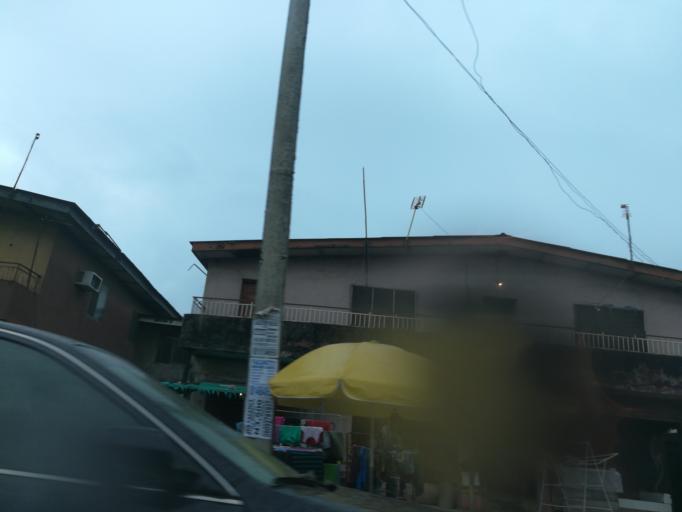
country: NG
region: Lagos
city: Oshodi
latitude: 6.5649
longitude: 3.3421
